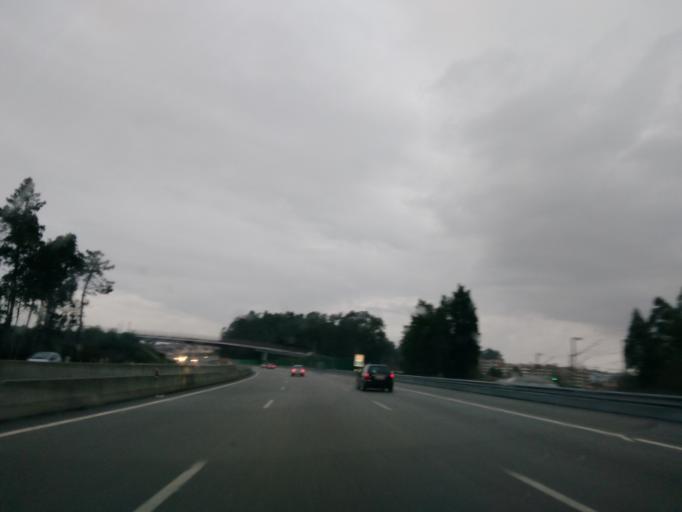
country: PT
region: Porto
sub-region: Trofa
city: Sao Romao do Coronado
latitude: 41.2723
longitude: -8.5597
